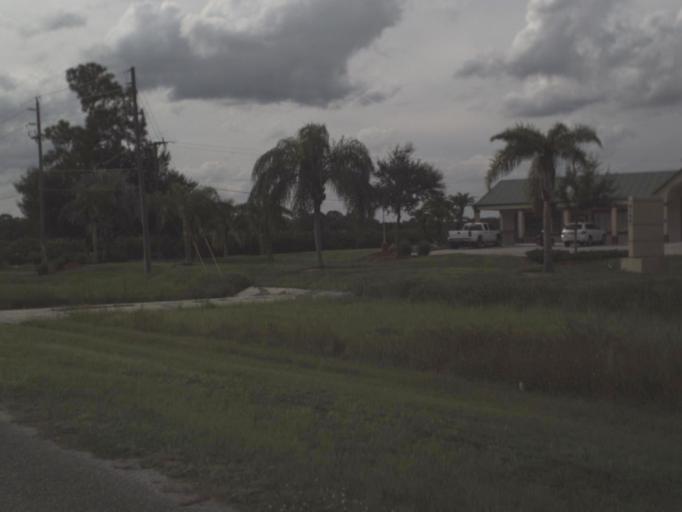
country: US
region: Florida
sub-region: Lee County
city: Alva
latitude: 26.7097
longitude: -81.5380
